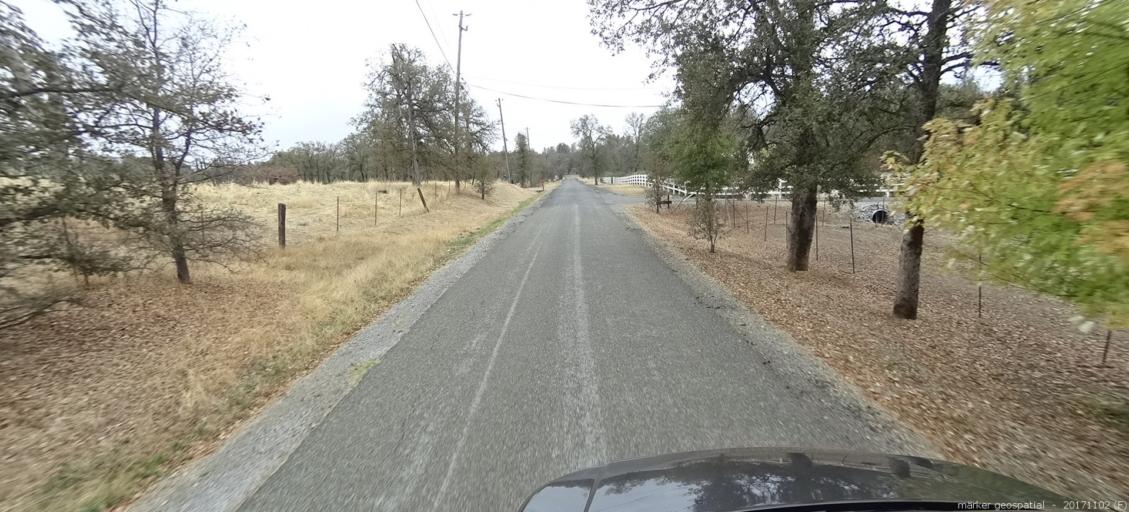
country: US
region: California
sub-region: Shasta County
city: Shasta Lake
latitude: 40.6580
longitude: -122.3148
